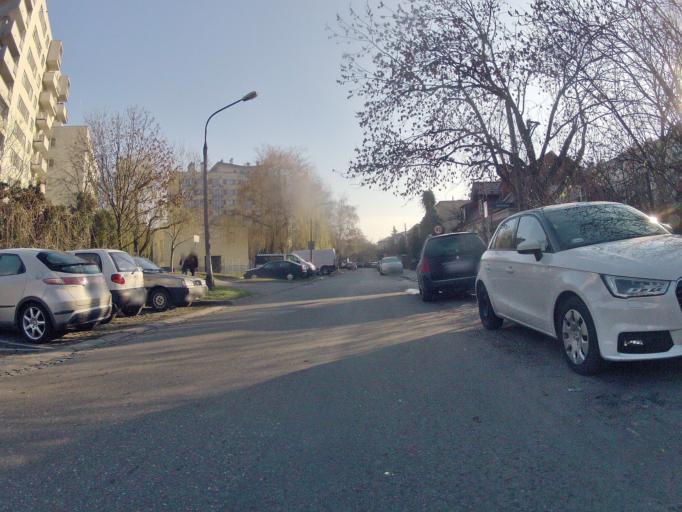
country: PL
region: Lesser Poland Voivodeship
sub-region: Krakow
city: Krakow
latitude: 50.0840
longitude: 19.9619
